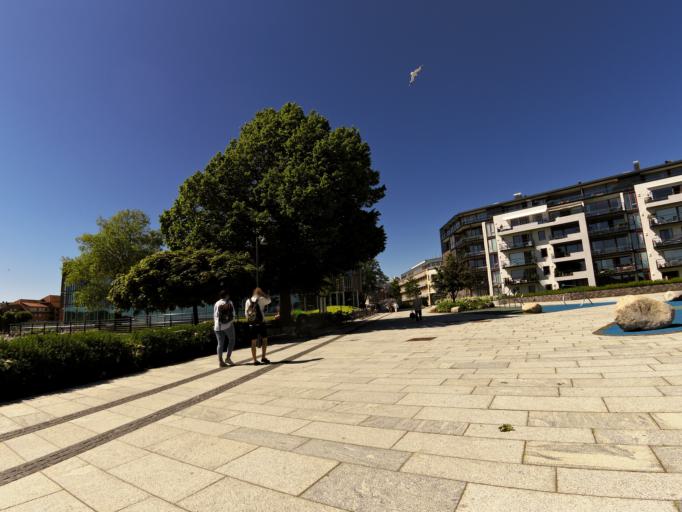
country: NO
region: Vest-Agder
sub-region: Kristiansand
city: Kristiansand
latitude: 58.1463
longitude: 8.0083
